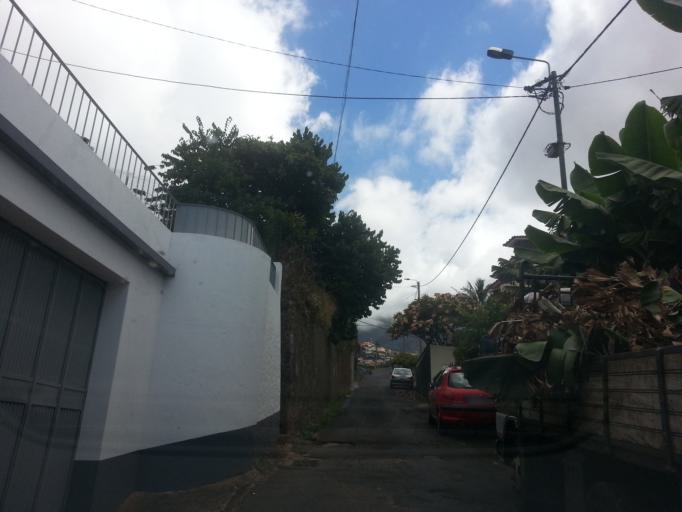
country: PT
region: Madeira
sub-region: Funchal
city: Nossa Senhora do Monte
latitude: 32.6666
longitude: -16.9312
